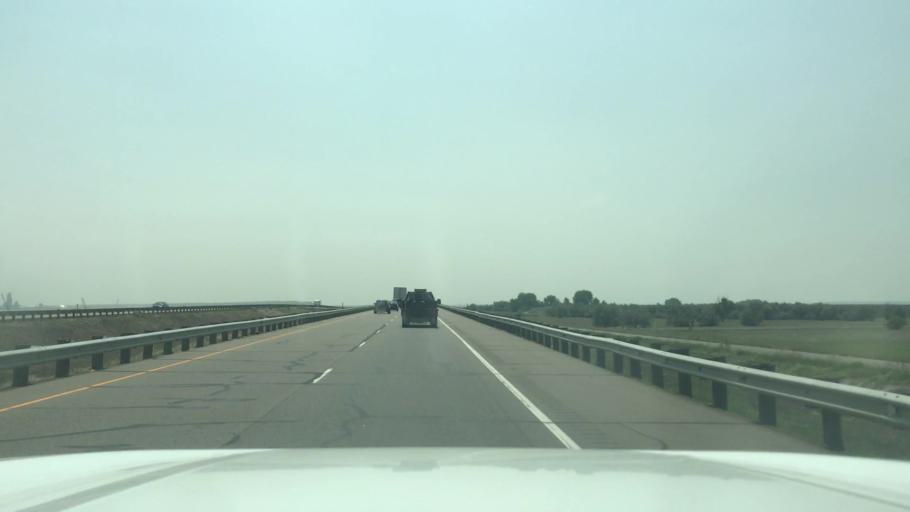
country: US
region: Colorado
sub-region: Pueblo County
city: Pueblo
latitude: 38.1858
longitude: -104.6337
